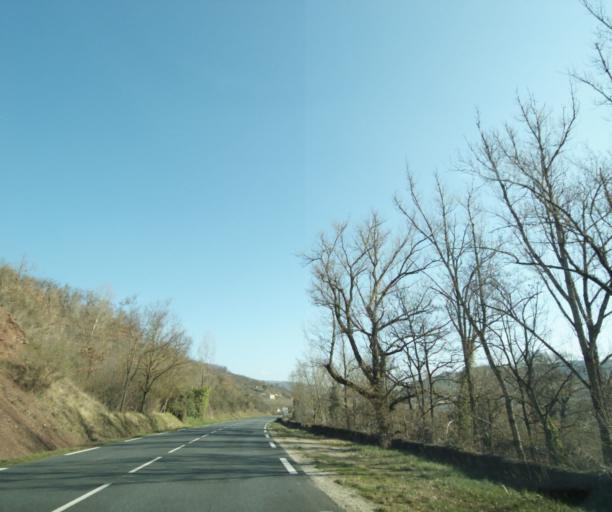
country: FR
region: Midi-Pyrenees
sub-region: Departement de l'Aveyron
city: Saint-Affrique
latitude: 43.9435
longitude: 2.8271
